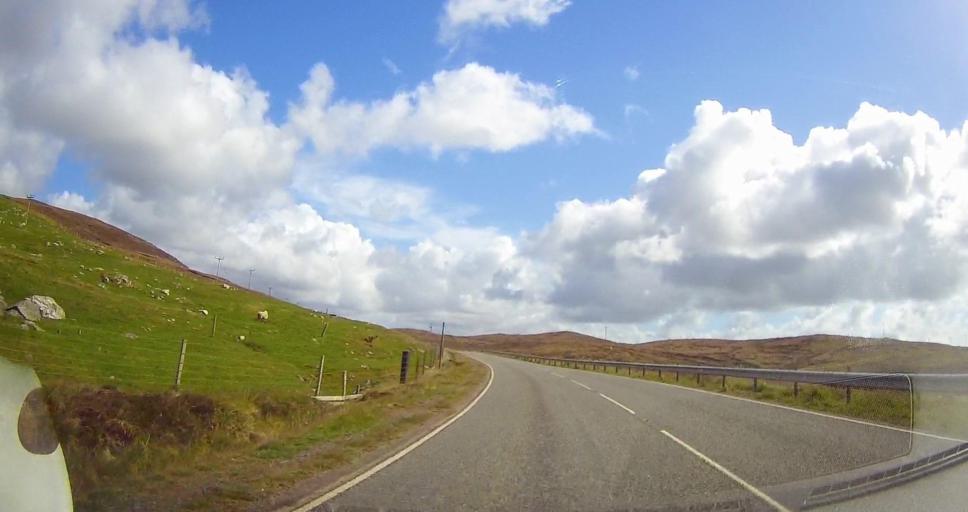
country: GB
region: Scotland
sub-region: Shetland Islands
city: Lerwick
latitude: 60.4632
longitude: -1.4049
